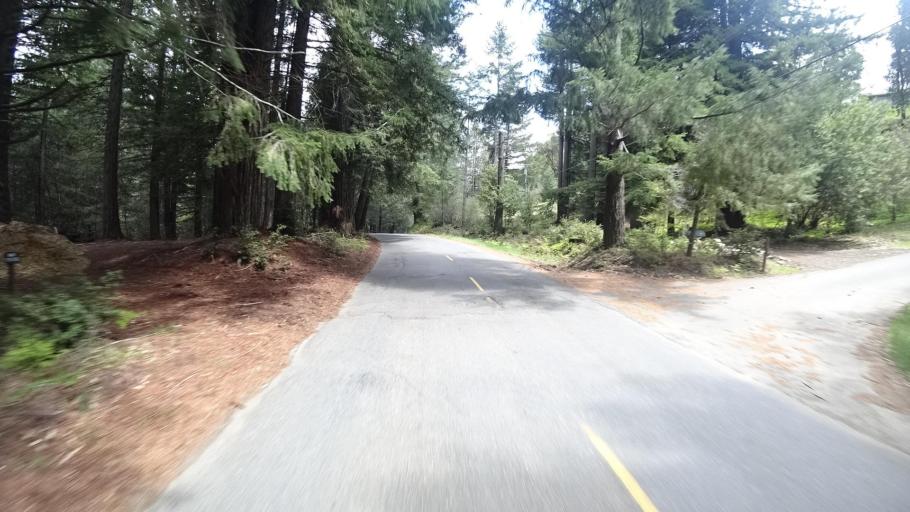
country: US
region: California
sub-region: Humboldt County
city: Redway
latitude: 40.0578
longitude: -123.9617
